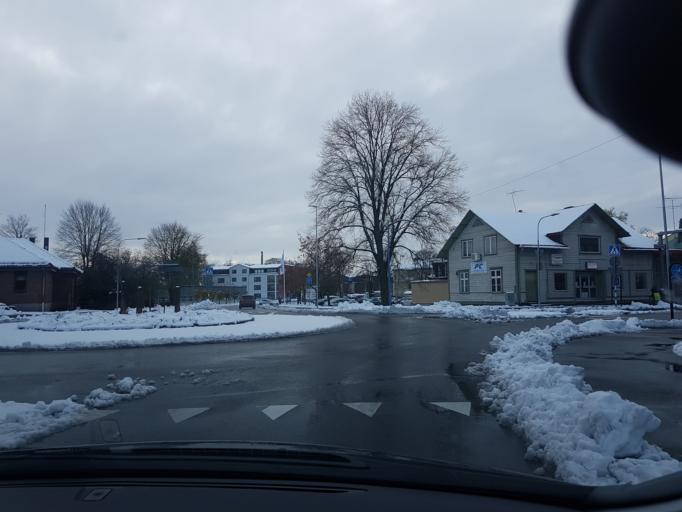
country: SE
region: Joenkoeping
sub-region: Vetlanda Kommun
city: Vetlanda
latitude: 57.4263
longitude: 15.0907
